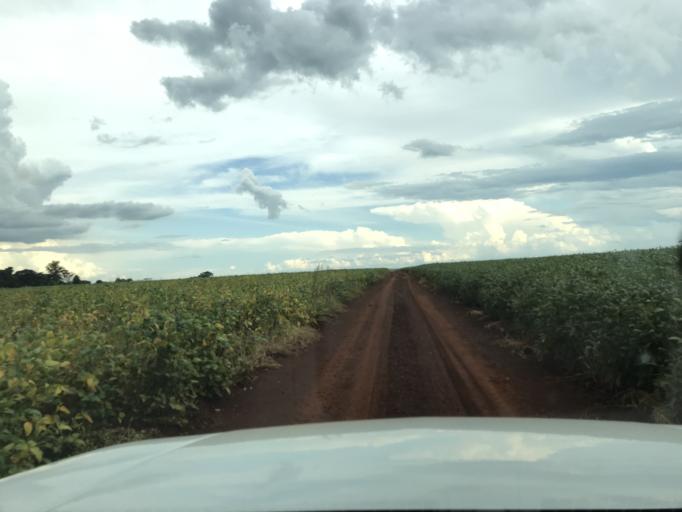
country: BR
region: Parana
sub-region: Palotina
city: Palotina
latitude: -24.2720
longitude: -53.7670
